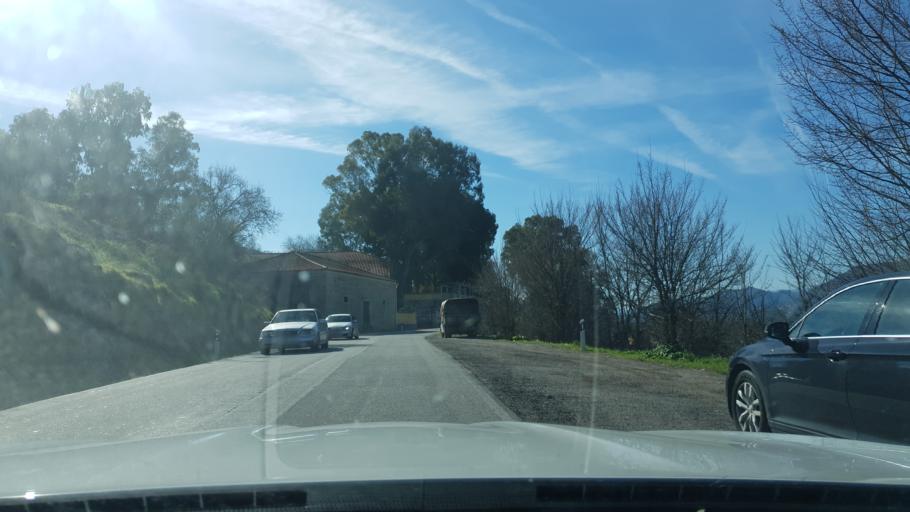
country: PT
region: Braganca
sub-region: Torre de Moncorvo
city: Torre de Moncorvo
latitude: 41.2178
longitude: -7.0919
